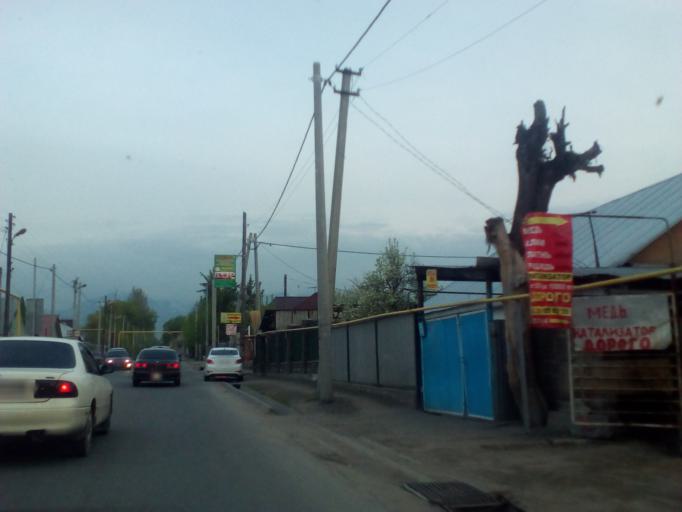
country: KZ
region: Almaty Qalasy
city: Almaty
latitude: 43.2328
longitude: 76.8257
